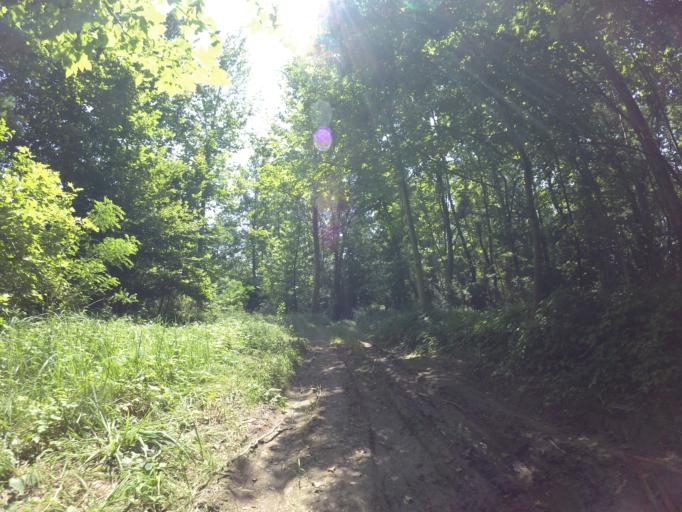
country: IT
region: Friuli Venezia Giulia
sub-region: Provincia di Udine
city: Rivignano
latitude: 45.8956
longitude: 13.0398
